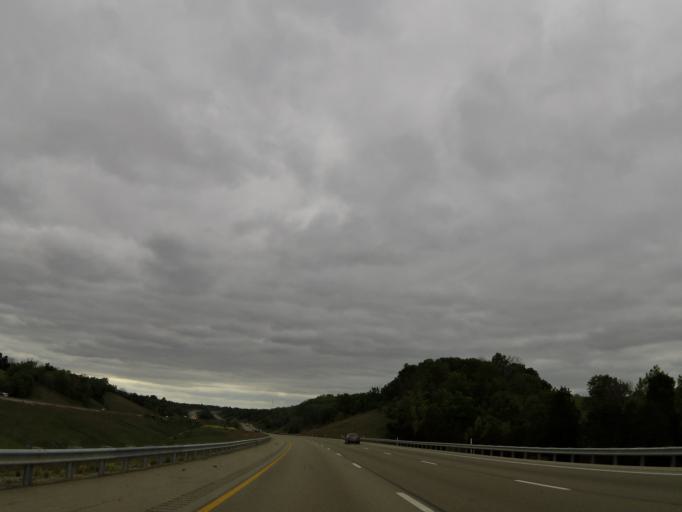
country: US
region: Kentucky
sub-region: Grant County
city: Williamstown
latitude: 38.5280
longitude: -84.5866
